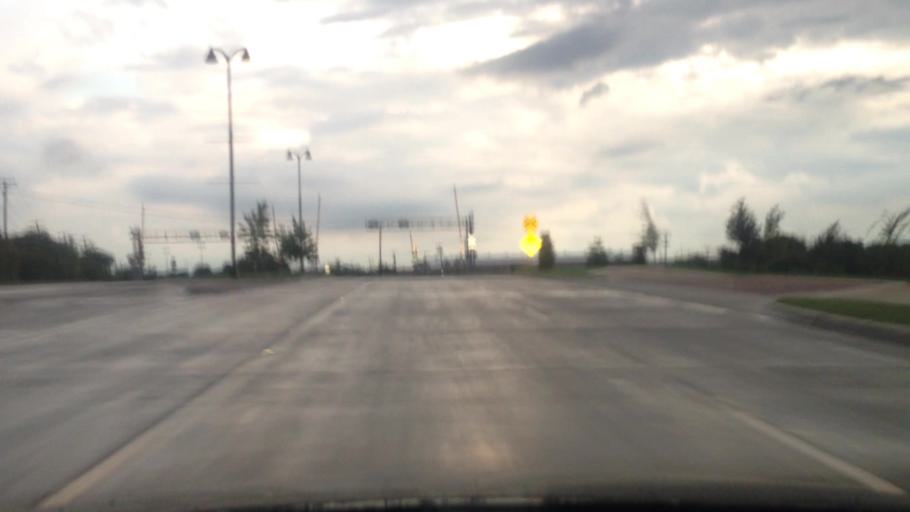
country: US
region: Texas
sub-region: Tarrant County
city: Arlington
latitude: 32.7402
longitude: -97.0837
